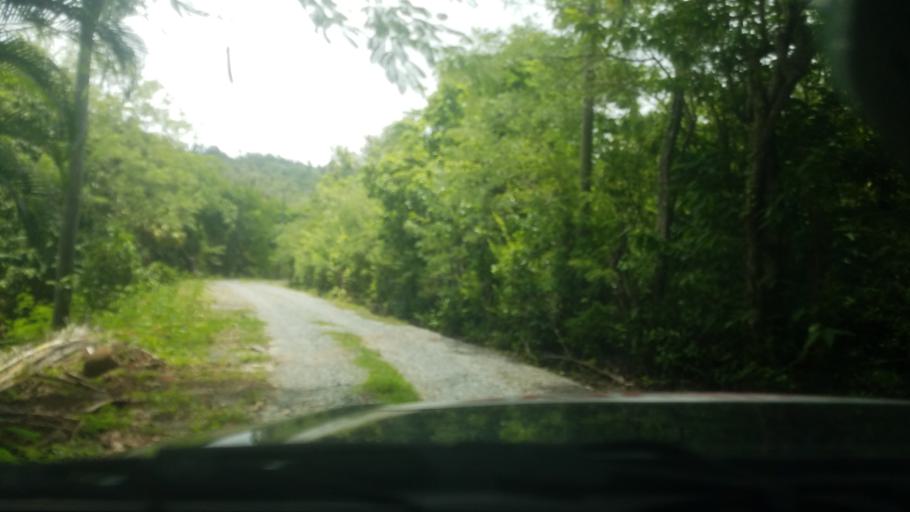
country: LC
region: Praslin
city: Praslin
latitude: 13.8667
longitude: -60.9046
